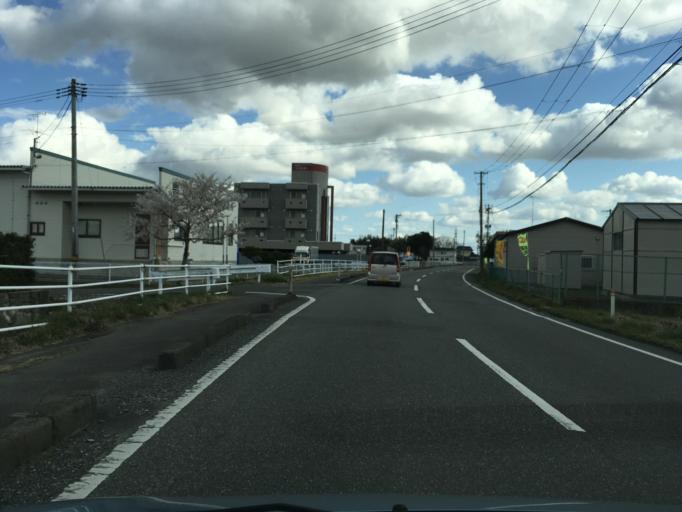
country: JP
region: Miyagi
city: Wakuya
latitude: 38.6705
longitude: 141.1941
